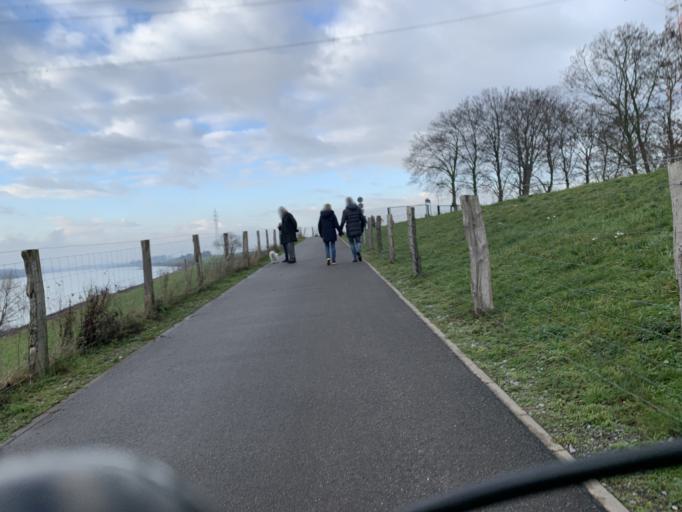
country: DE
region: North Rhine-Westphalia
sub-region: Regierungsbezirk Dusseldorf
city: Meerbusch
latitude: 51.3351
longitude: 6.7152
